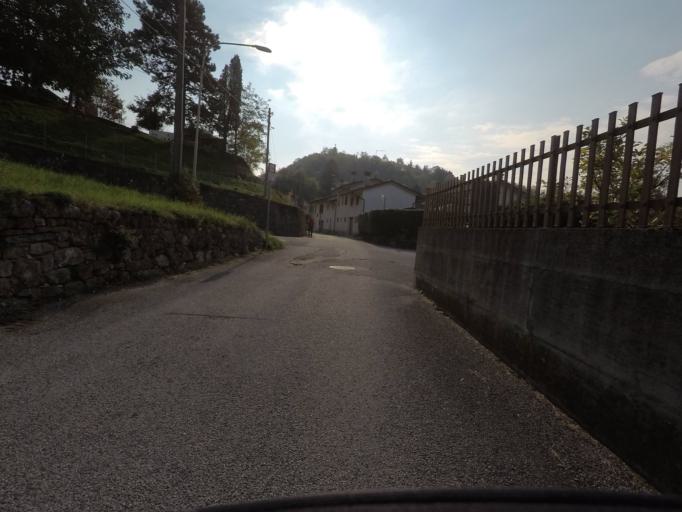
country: IT
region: Friuli Venezia Giulia
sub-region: Provincia di Udine
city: Artegna
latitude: 46.2445
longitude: 13.1504
